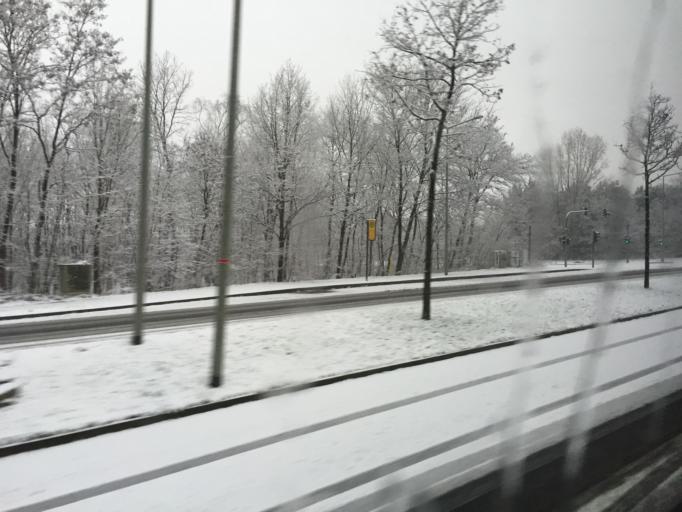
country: DE
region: Saxony
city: Albertstadt
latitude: 51.0991
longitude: 13.7361
